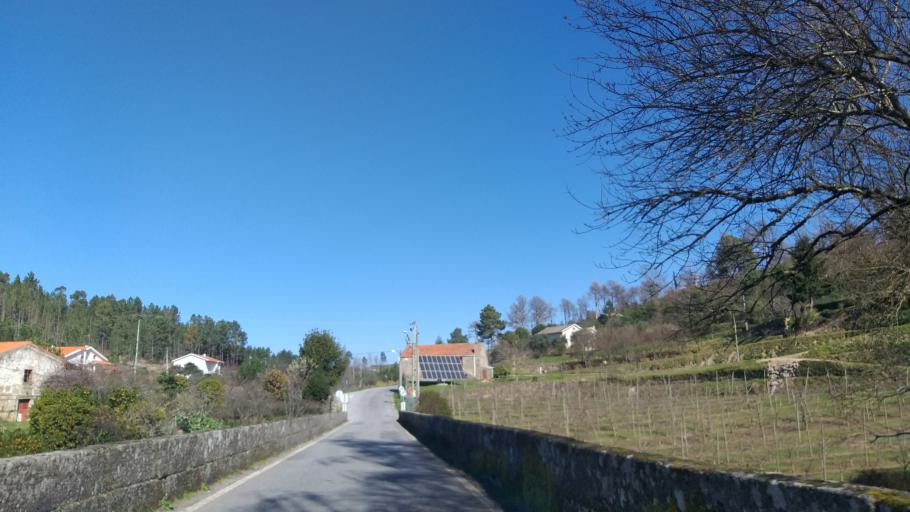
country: PT
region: Guarda
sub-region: Manteigas
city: Manteigas
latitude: 40.4765
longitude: -7.6190
